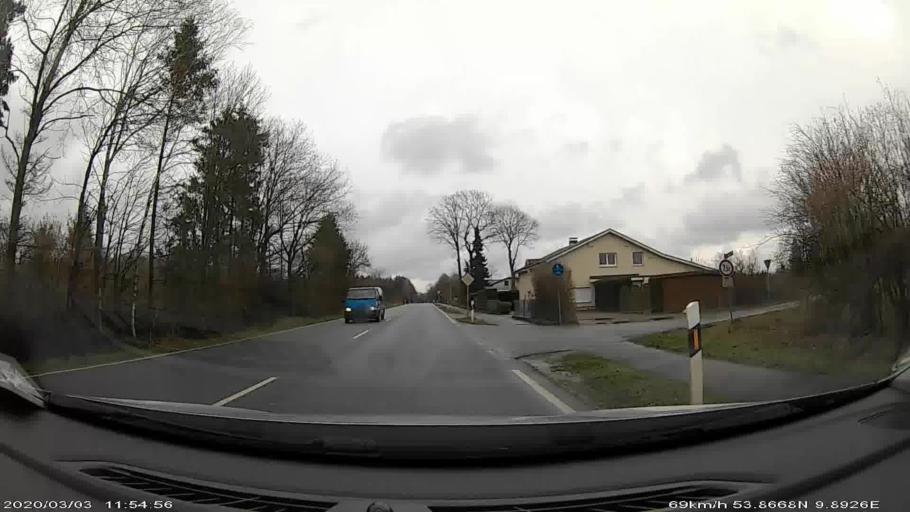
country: DE
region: Schleswig-Holstein
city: Lentfohrden
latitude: 53.8664
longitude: 9.8967
